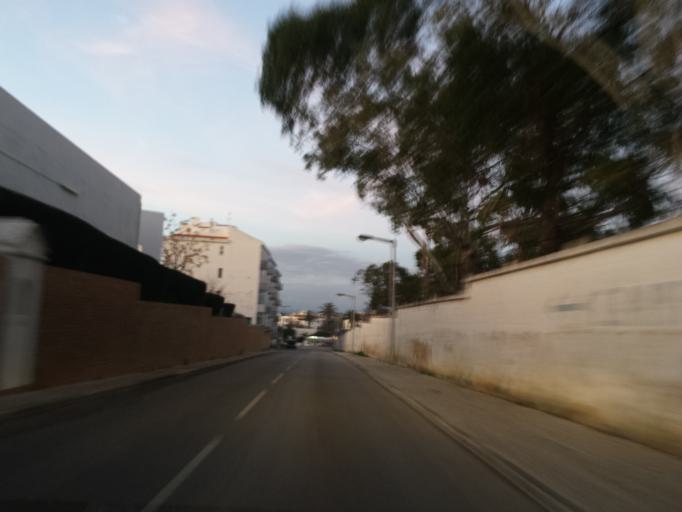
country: PT
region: Faro
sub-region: Lagos
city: Lagos
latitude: 37.0934
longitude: -8.6720
